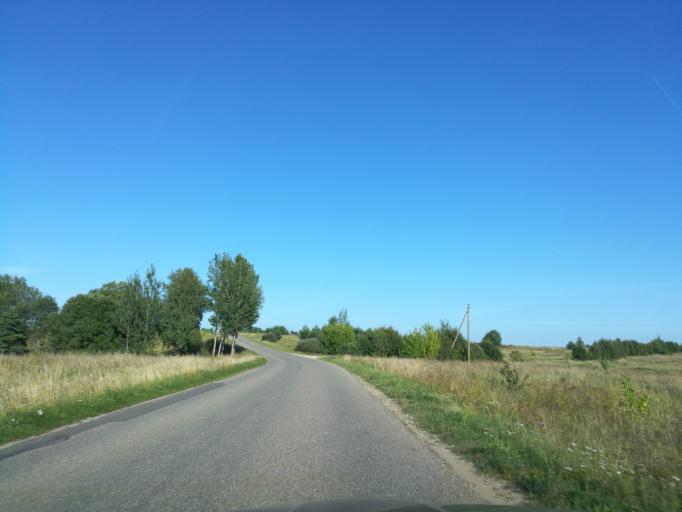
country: LT
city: Trakai
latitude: 54.6732
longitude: 24.9362
